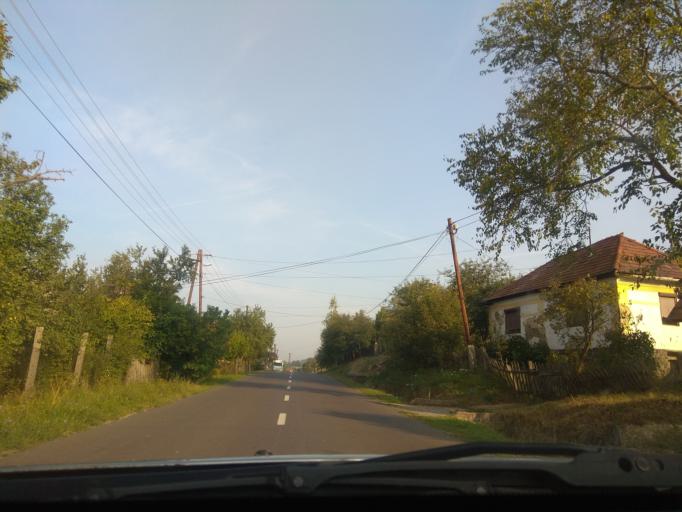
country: HU
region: Borsod-Abauj-Zemplen
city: Rudabanya
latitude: 48.4028
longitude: 20.5247
